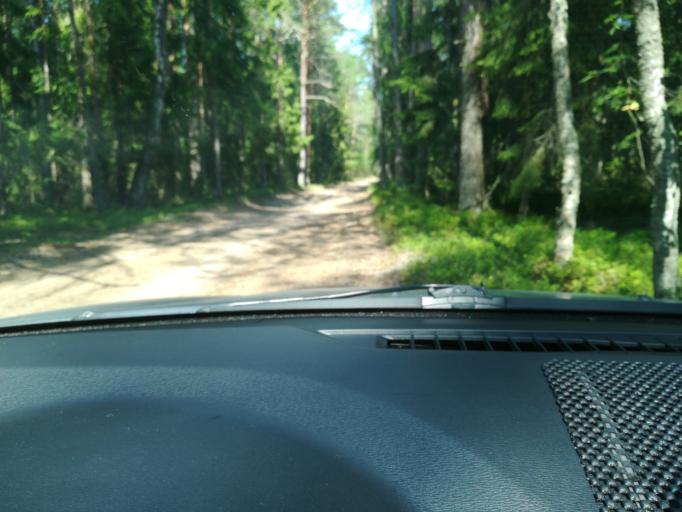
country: RU
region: Leningrad
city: Ust'-Luga
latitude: 59.7402
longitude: 28.1876
